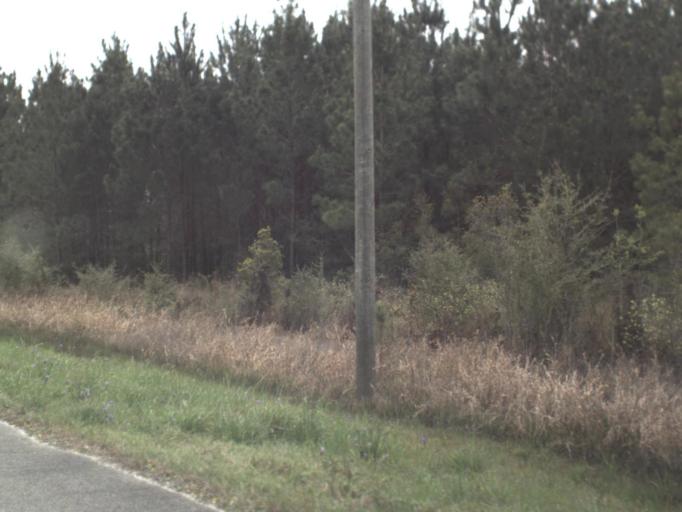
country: US
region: Florida
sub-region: Gulf County
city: Wewahitchka
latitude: 29.9875
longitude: -85.1687
